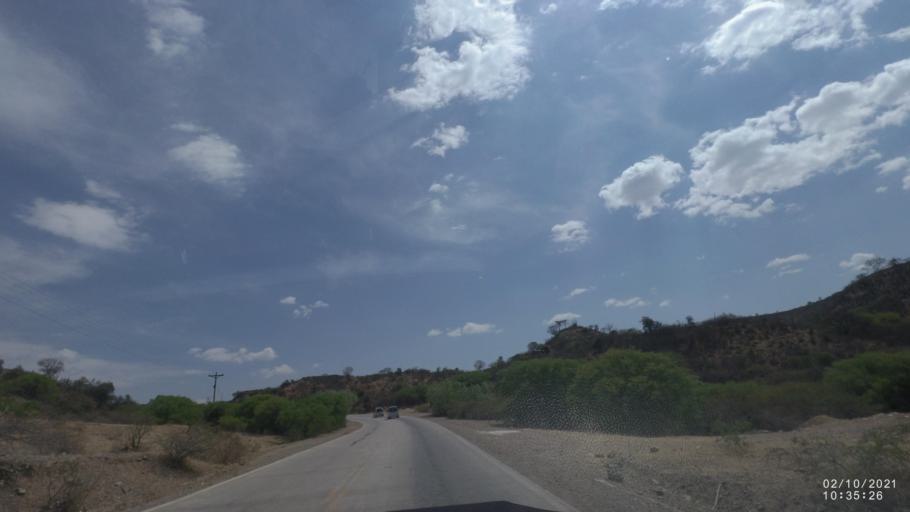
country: BO
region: Cochabamba
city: Capinota
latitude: -17.6611
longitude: -66.2576
